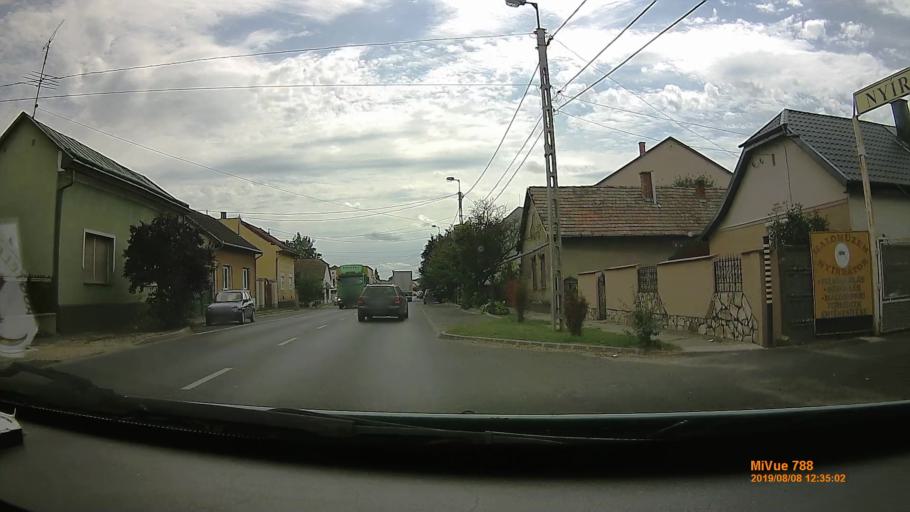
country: HU
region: Szabolcs-Szatmar-Bereg
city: Nyirbator
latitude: 47.8368
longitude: 22.1251
